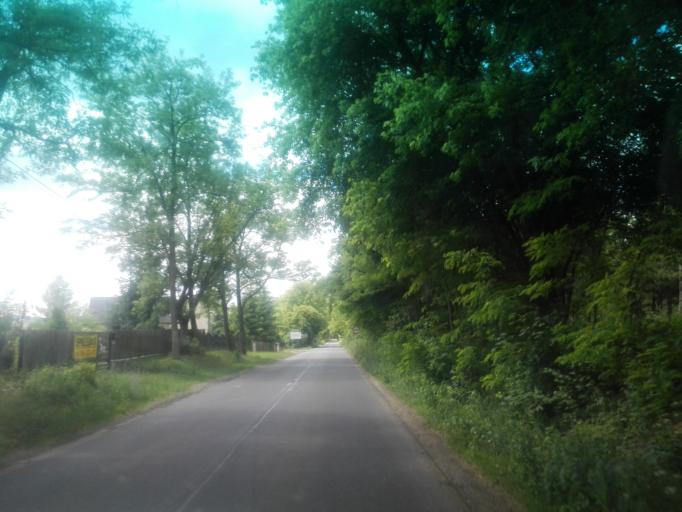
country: PL
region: Silesian Voivodeship
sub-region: Powiat czestochowski
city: Olsztyn
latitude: 50.7676
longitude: 19.2745
